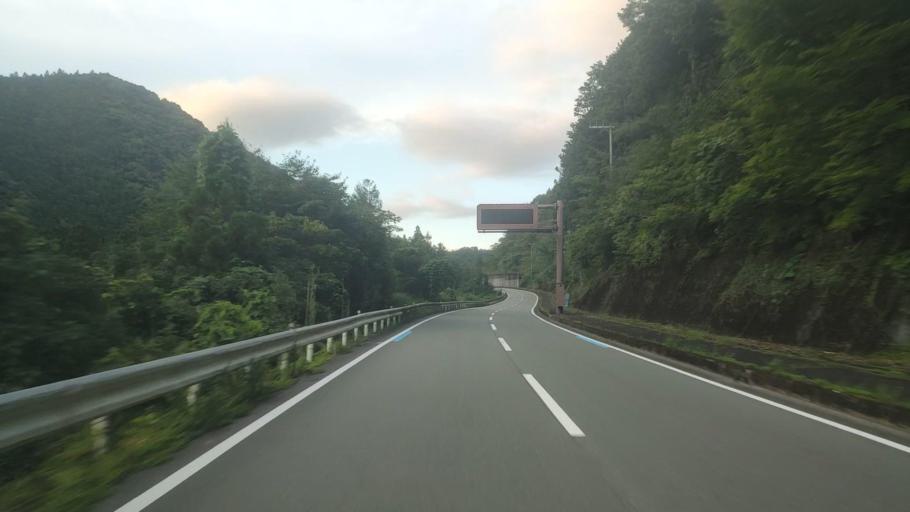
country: JP
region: Wakayama
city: Shingu
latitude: 33.8203
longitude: 135.7693
